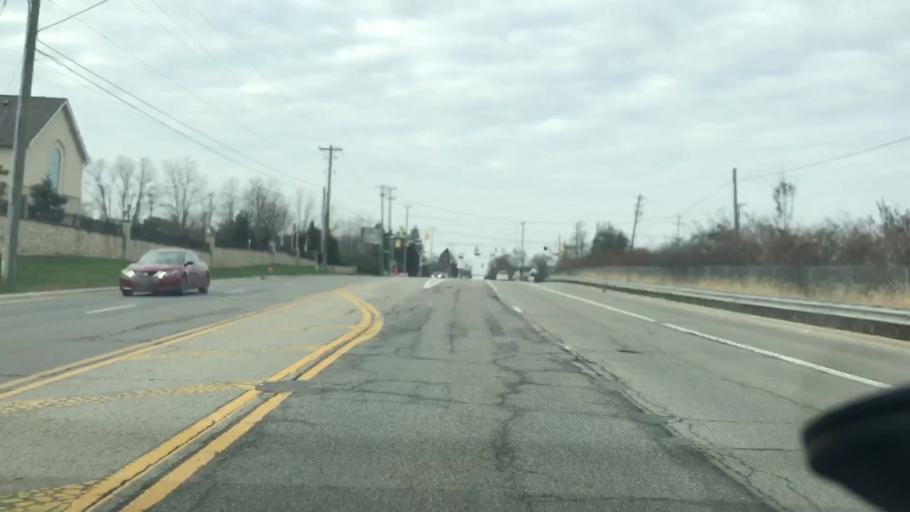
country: US
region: Ohio
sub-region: Franklin County
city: Upper Arlington
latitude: 39.9957
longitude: -83.0835
